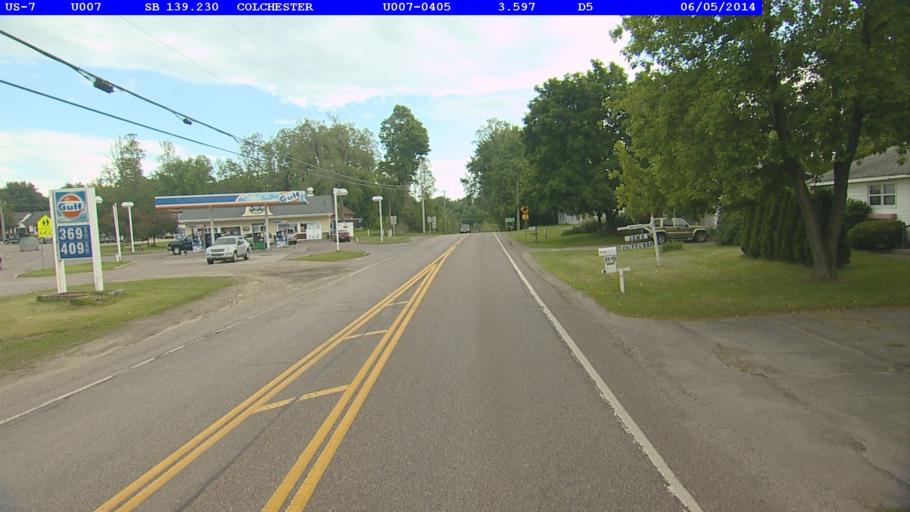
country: US
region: Vermont
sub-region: Chittenden County
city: Colchester
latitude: 44.5506
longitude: -73.1640
